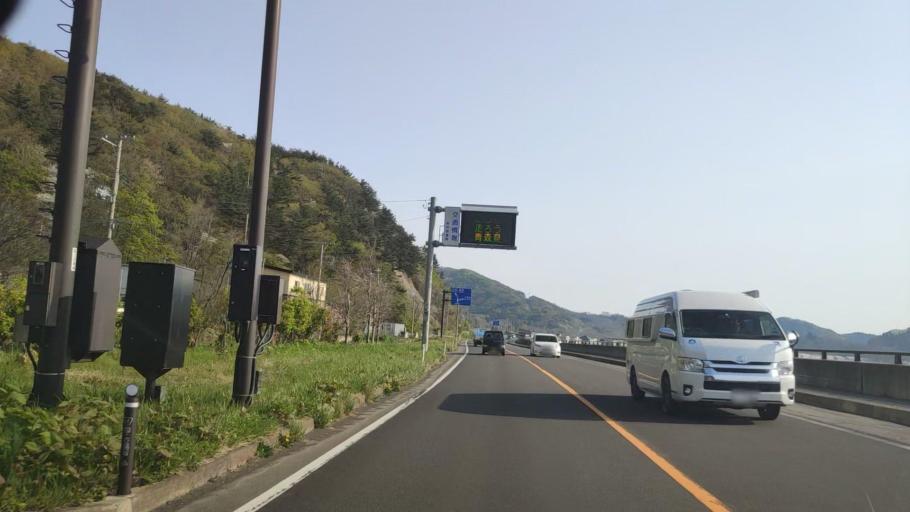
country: JP
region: Aomori
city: Aomori Shi
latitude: 40.8819
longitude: 140.8503
